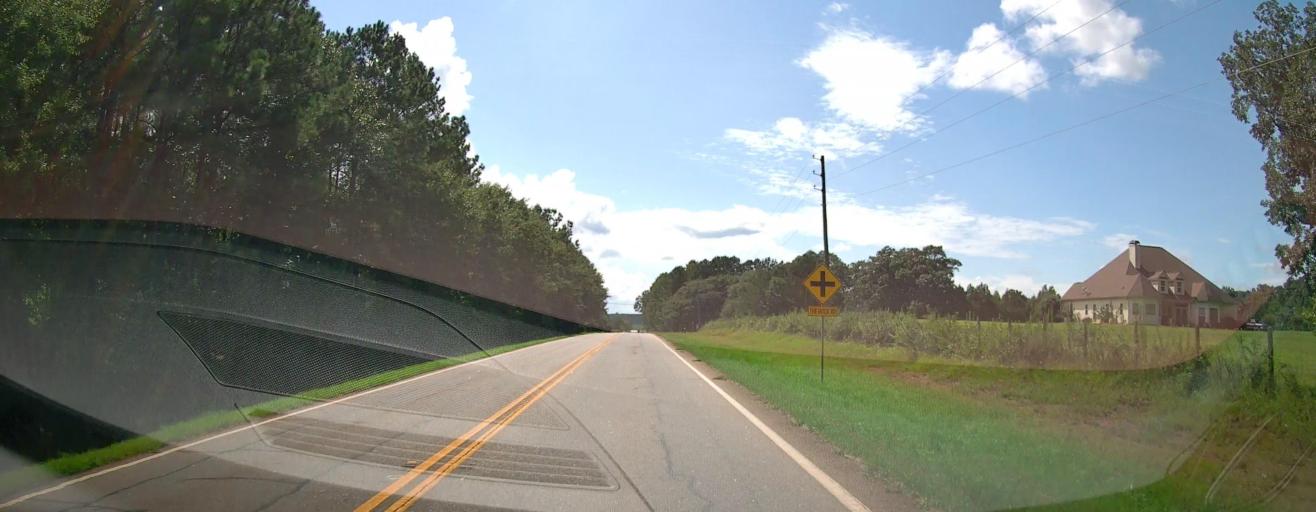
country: US
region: Georgia
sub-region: Upson County
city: Thomaston
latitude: 32.9214
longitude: -84.2300
